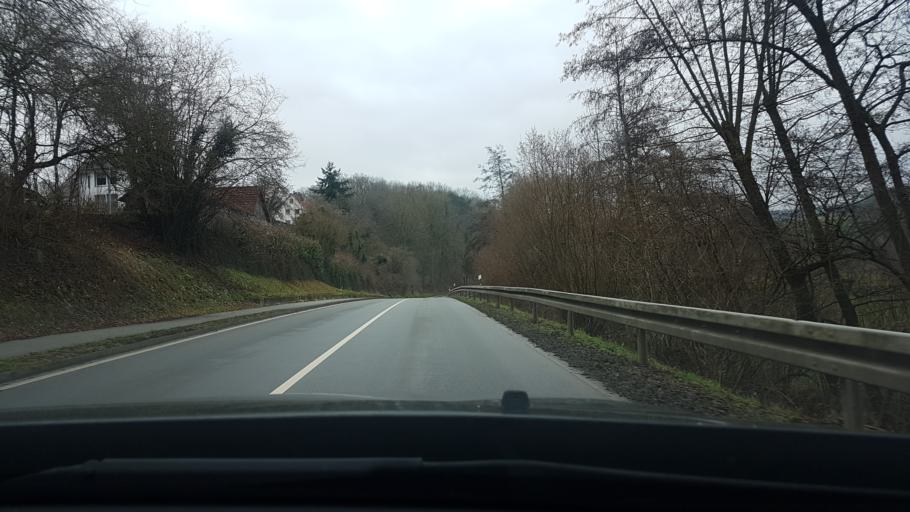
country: DE
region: Hesse
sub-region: Regierungsbezirk Kassel
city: Volkmarsen
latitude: 51.3962
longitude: 9.0715
